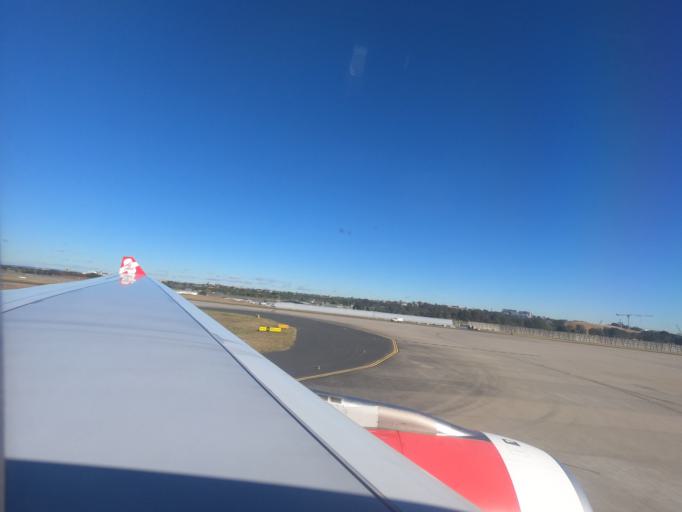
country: AU
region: New South Wales
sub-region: Rockdale
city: Arncliffe
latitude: -33.9419
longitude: 151.1646
